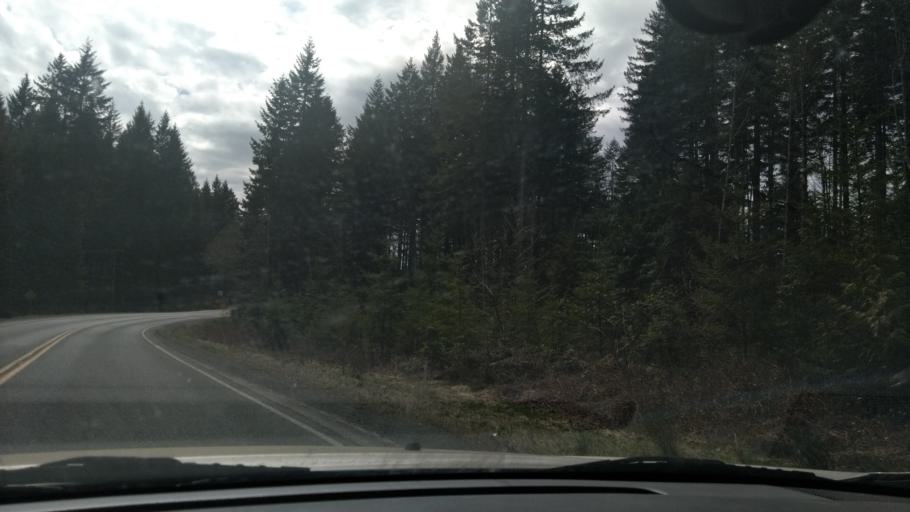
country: CA
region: British Columbia
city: Campbell River
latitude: 49.9778
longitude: -125.4386
